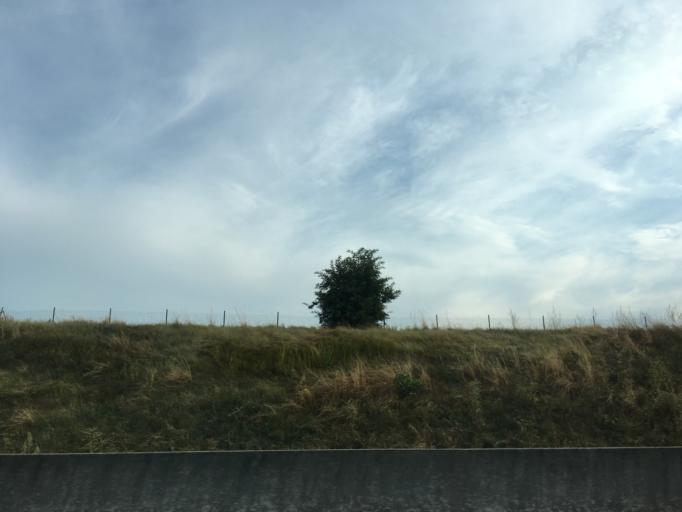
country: FR
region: Ile-de-France
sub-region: Departement des Yvelines
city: Montesson
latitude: 48.9146
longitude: 2.1455
